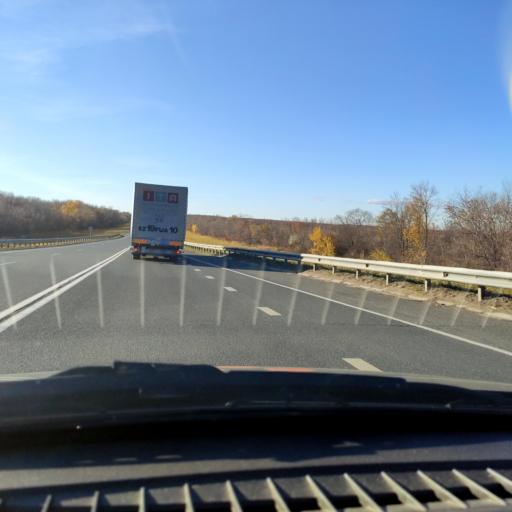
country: RU
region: Samara
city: Mezhdurechensk
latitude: 53.2568
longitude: 49.1219
